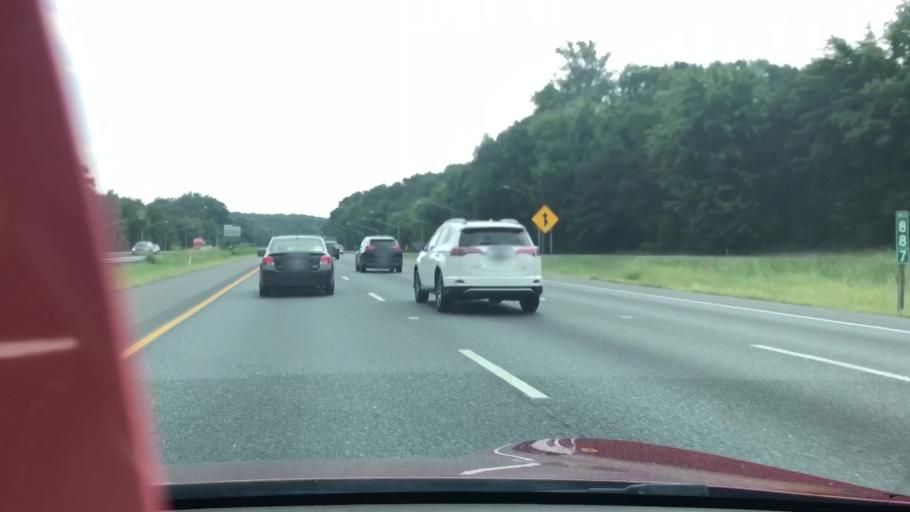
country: US
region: Maryland
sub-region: Harford County
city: Havre de Grace
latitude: 39.5676
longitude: -76.1396
